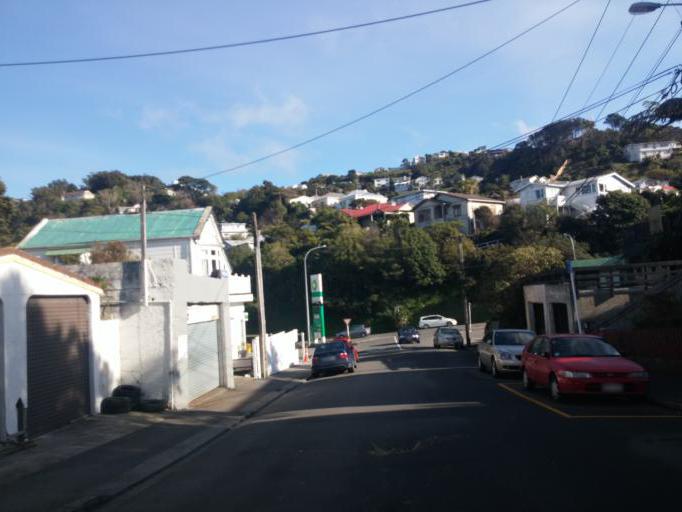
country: NZ
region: Wellington
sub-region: Wellington City
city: Brooklyn
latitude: -41.3065
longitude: 174.7641
